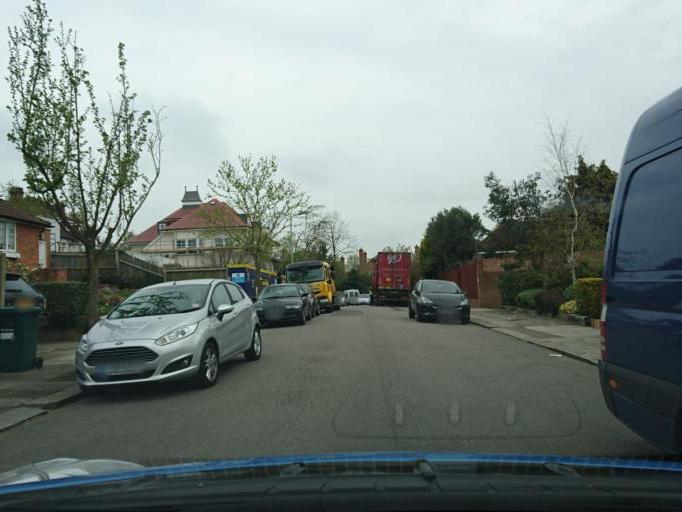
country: GB
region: England
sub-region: Greater London
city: Barnet
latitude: 51.6301
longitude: -0.1865
